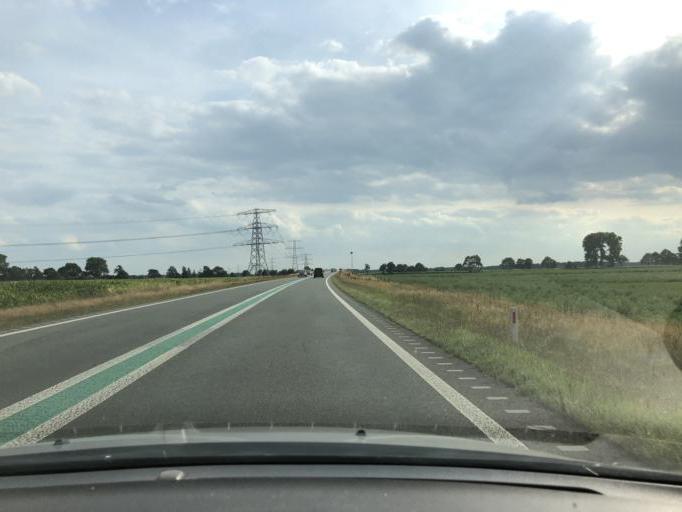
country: NL
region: Drenthe
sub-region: Gemeente Emmen
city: Emmen
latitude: 52.8068
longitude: 6.8576
